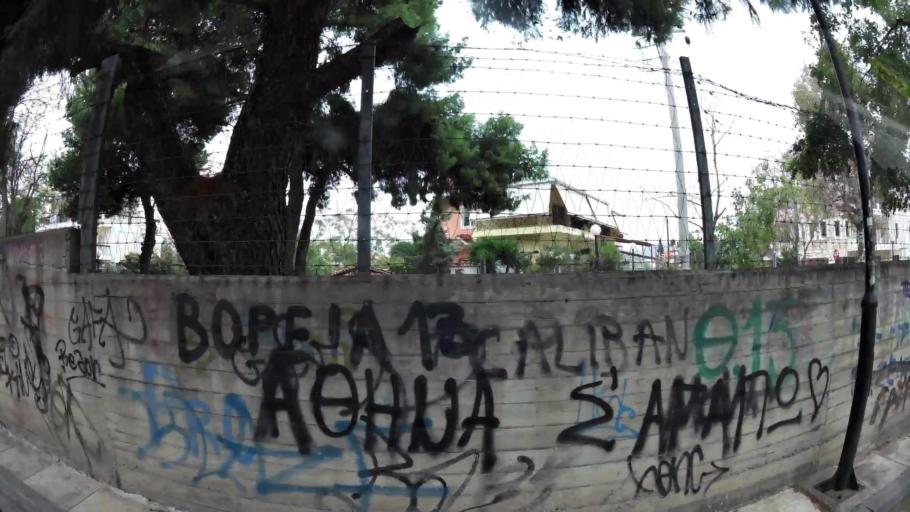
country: GR
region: Attica
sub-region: Nomarchia Athinas
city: Irakleio
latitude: 38.0452
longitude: 23.7787
